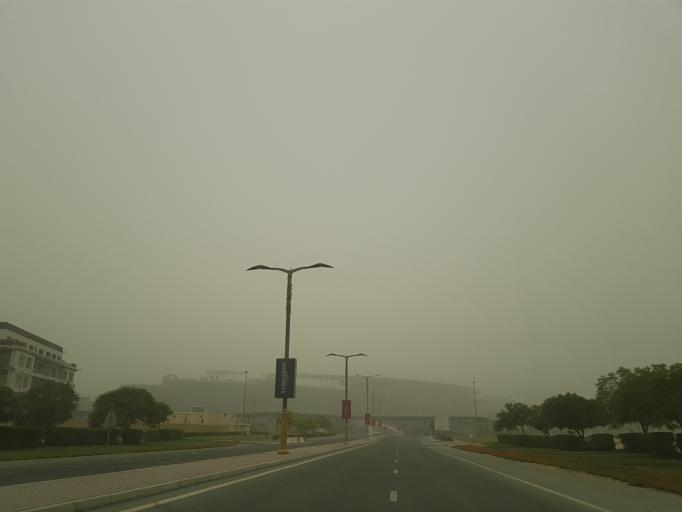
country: AE
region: Dubai
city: Dubai
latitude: 25.1639
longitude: 55.3011
